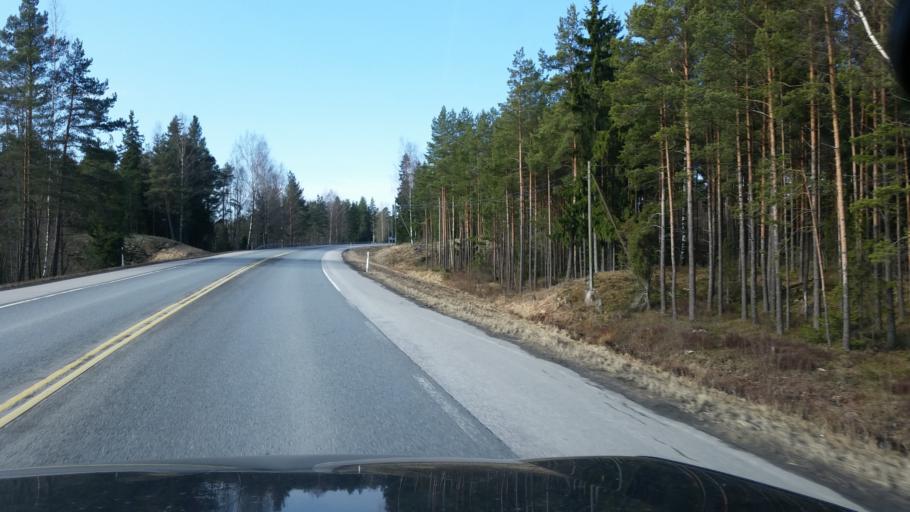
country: FI
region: Uusimaa
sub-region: Raaseporin
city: Inga
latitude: 60.0641
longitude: 24.0960
